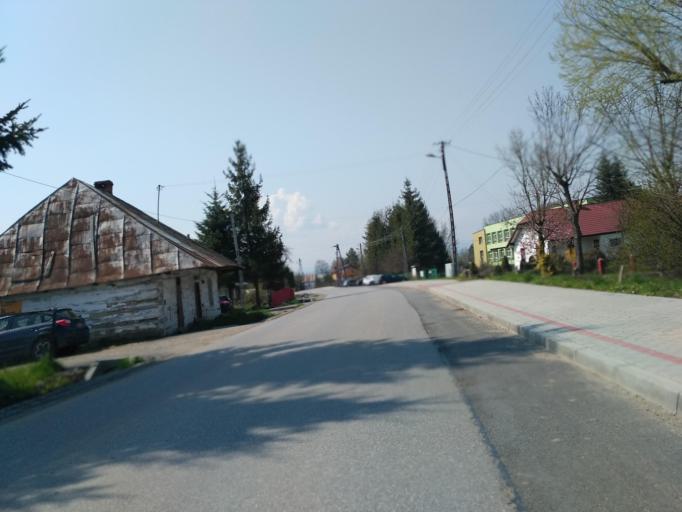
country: PL
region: Subcarpathian Voivodeship
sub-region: Powiat sanocki
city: Zarszyn
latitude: 49.6166
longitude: 22.0170
